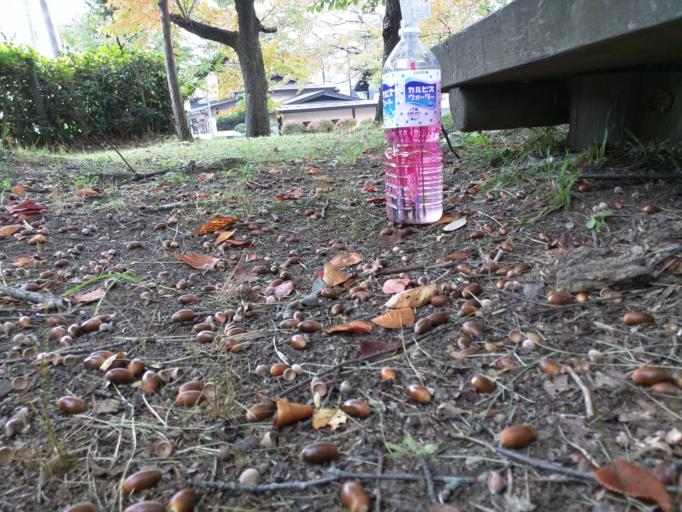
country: JP
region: Fukushima
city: Kitakata
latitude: 37.4976
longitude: 139.9474
